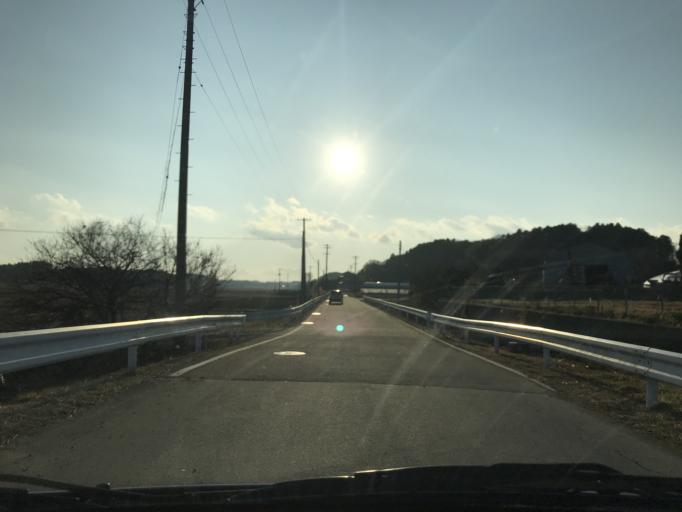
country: JP
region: Miyagi
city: Wakuya
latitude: 38.7198
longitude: 141.1406
